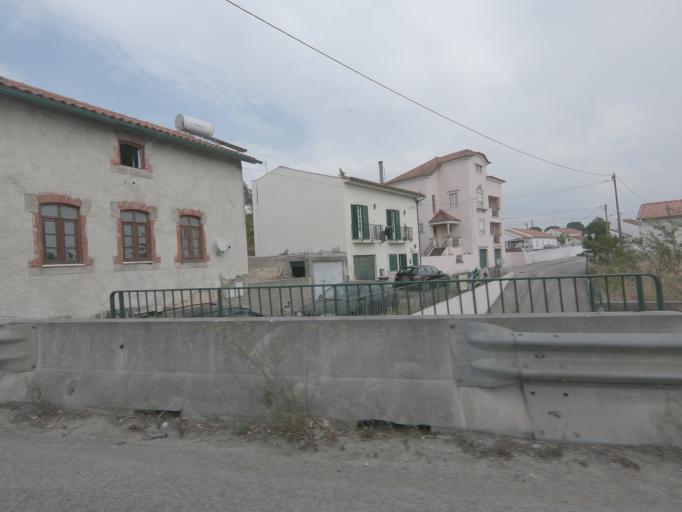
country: PT
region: Coimbra
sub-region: Condeixa-A-Nova
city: Condeixa-a-Nova
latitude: 40.1372
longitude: -8.4687
